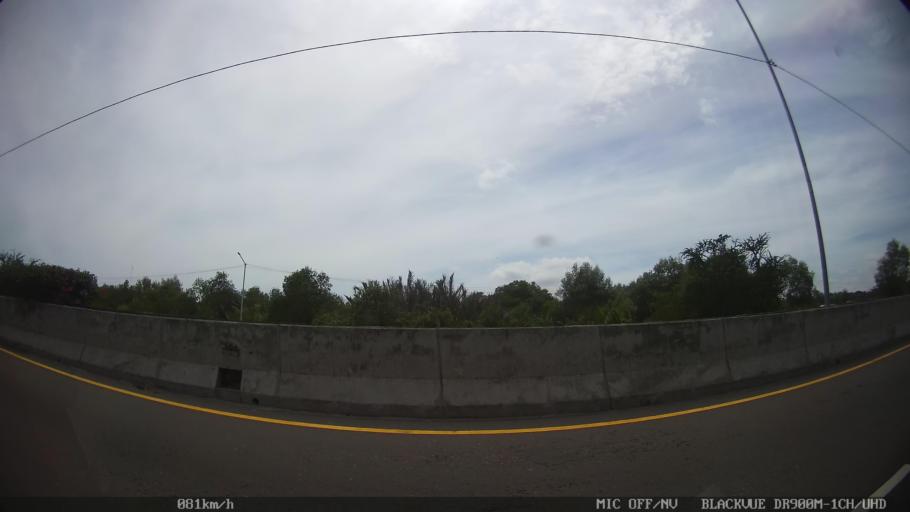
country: ID
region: North Sumatra
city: Belawan
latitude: 3.7634
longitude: 98.6833
